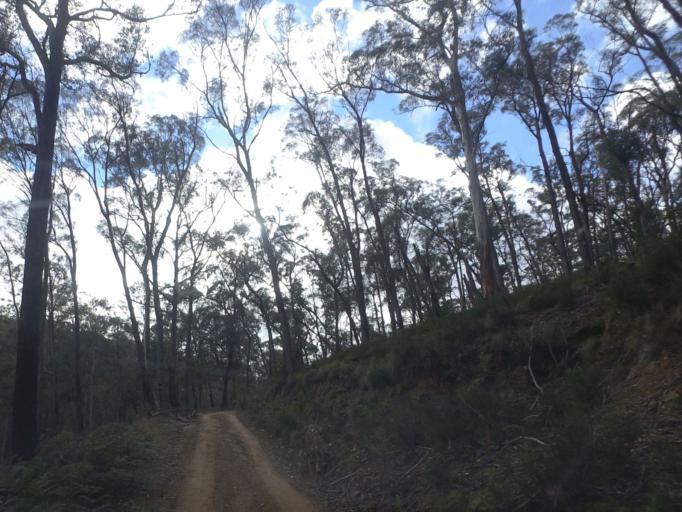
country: AU
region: Victoria
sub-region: Moorabool
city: Bacchus Marsh
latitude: -37.4627
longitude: 144.3113
